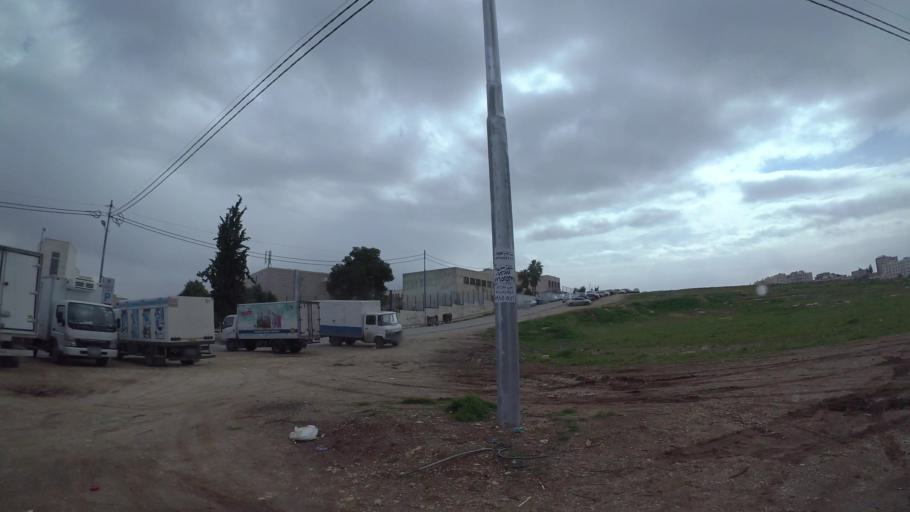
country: JO
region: Amman
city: Umm as Summaq
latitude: 31.8902
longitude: 35.8445
